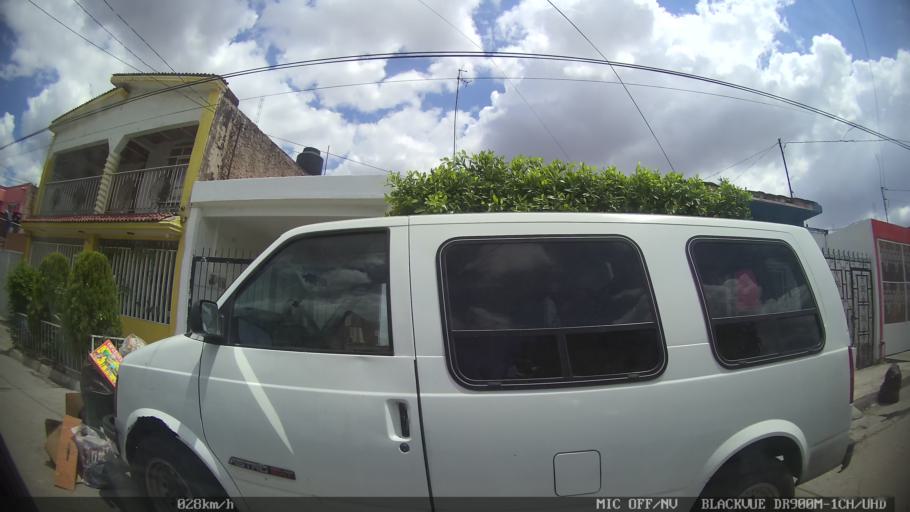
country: MX
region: Jalisco
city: Tlaquepaque
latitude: 20.6501
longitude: -103.2754
